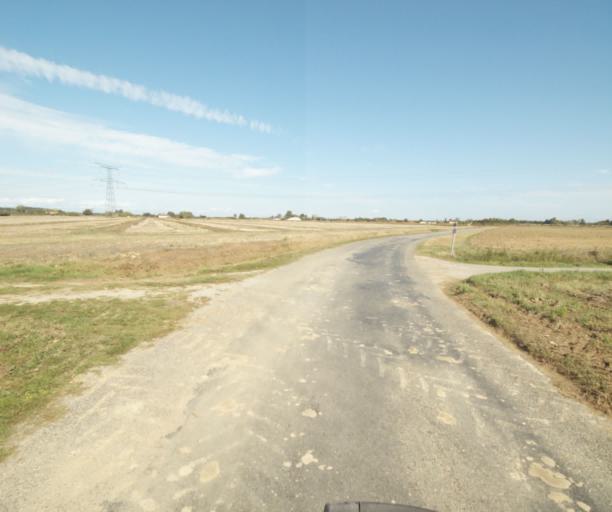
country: FR
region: Midi-Pyrenees
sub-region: Departement du Tarn-et-Garonne
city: Verdun-sur-Garonne
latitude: 43.8481
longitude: 1.2038
